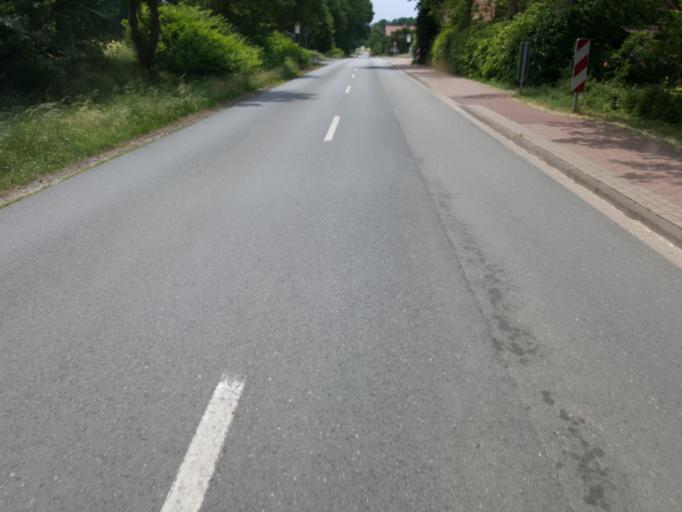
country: DE
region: Lower Saxony
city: Husum
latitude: 52.5799
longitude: 9.2485
